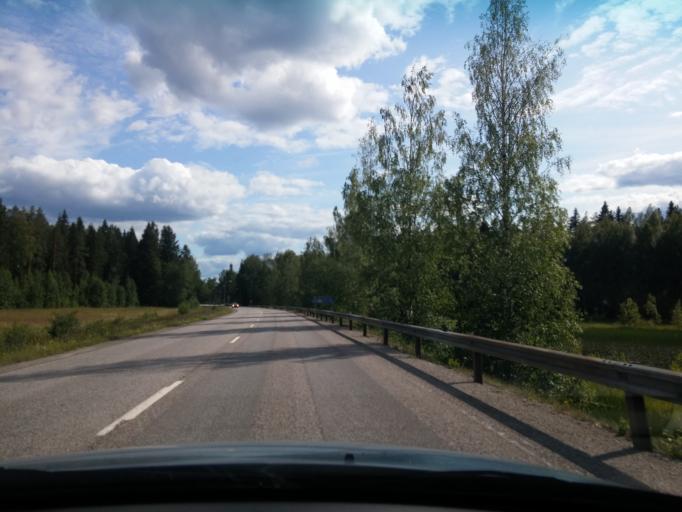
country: FI
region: Central Finland
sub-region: Keuruu
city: Keuruu
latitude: 62.2738
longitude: 24.6881
